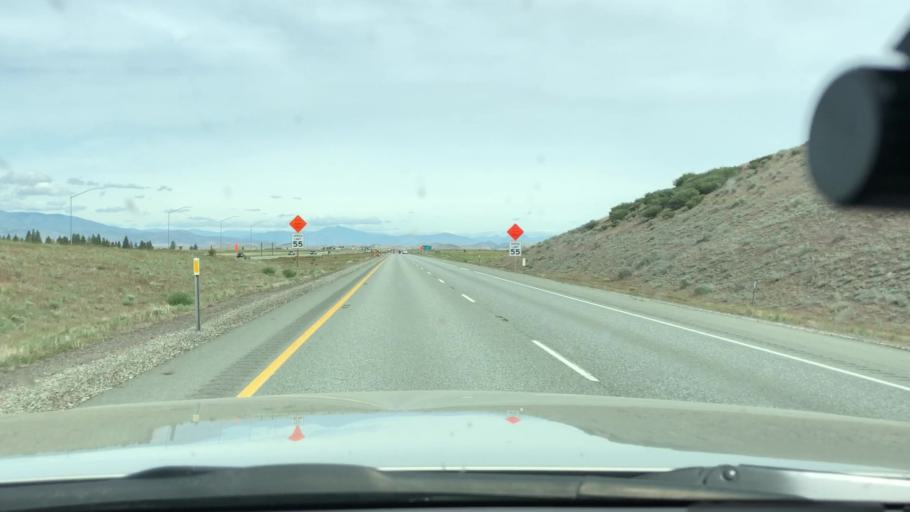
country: US
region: California
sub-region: Siskiyou County
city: Weed
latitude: 41.4538
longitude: -122.4436
